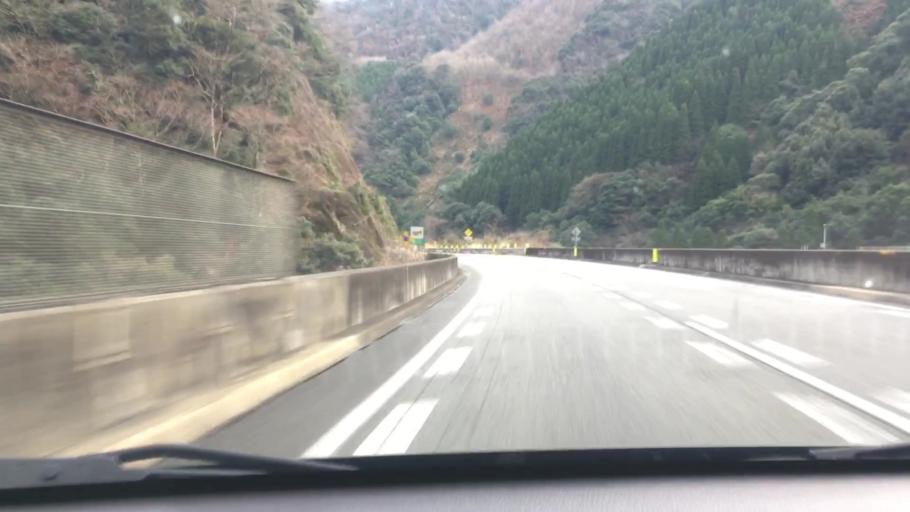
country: JP
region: Kumamoto
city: Hitoyoshi
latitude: 32.3332
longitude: 130.7387
